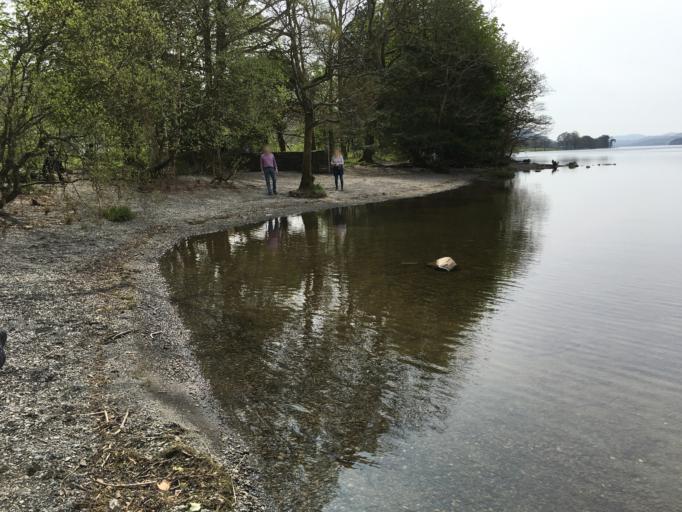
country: GB
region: England
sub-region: Cumbria
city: Ambleside
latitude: 54.3719
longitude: -3.0543
